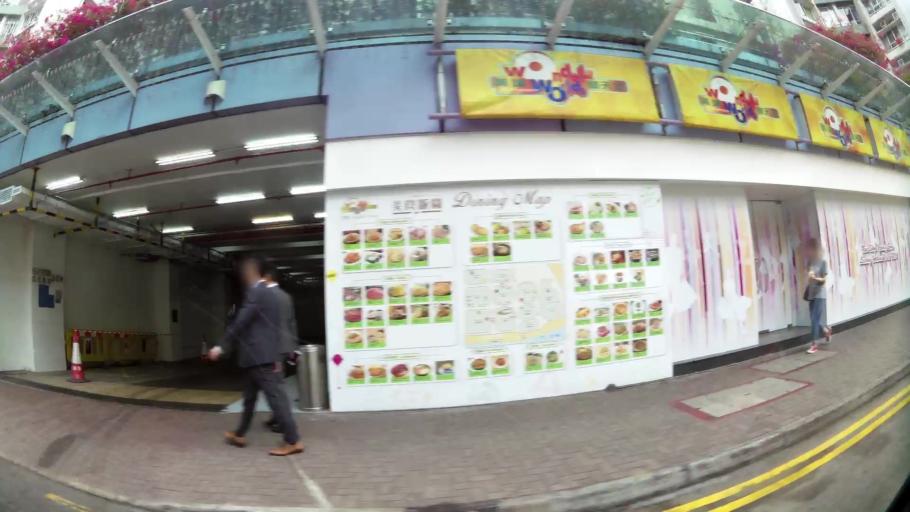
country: HK
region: Kowloon City
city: Kowloon
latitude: 22.3026
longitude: 114.1912
